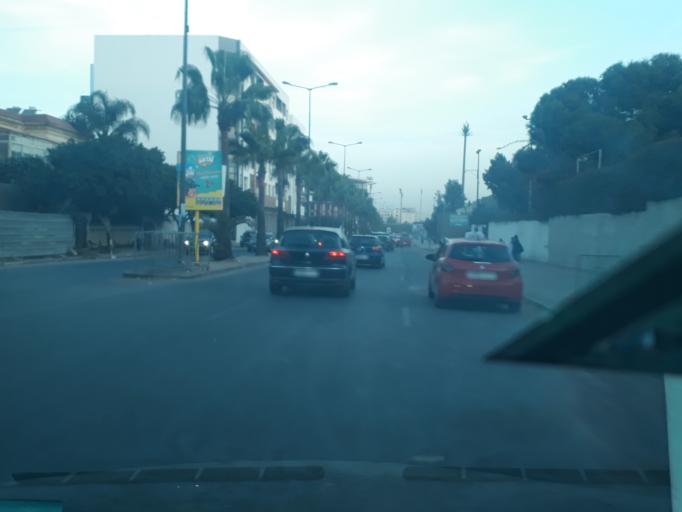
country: MA
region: Grand Casablanca
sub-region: Casablanca
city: Casablanca
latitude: 33.5788
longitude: -7.6459
